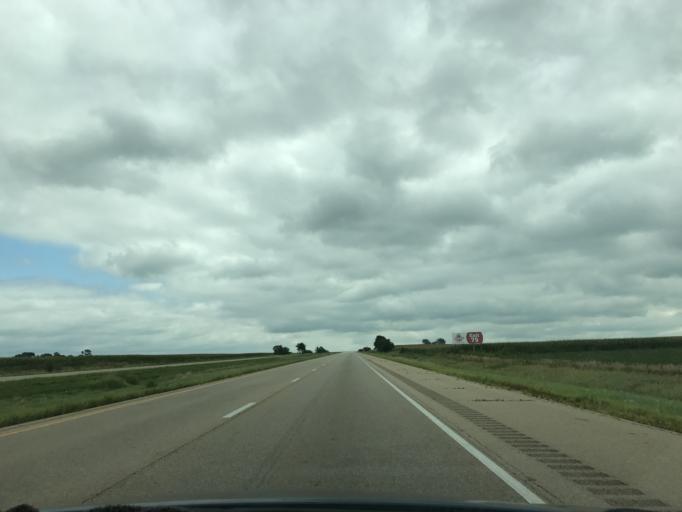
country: US
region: Illinois
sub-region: Bureau County
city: Depue
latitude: 41.4001
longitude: -89.3372
